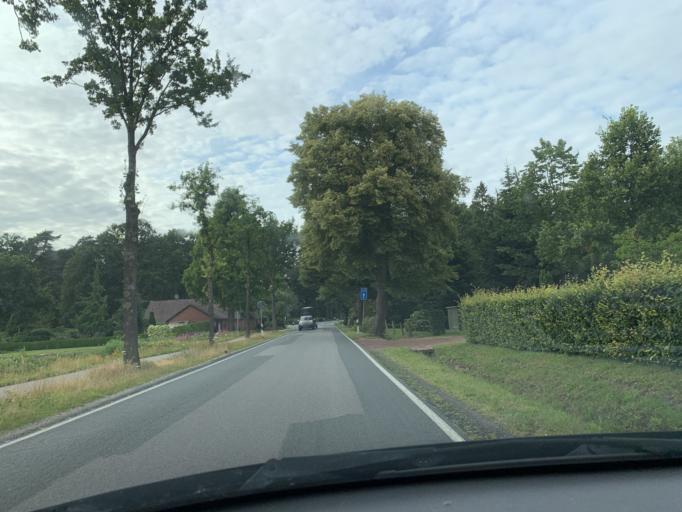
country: DE
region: Lower Saxony
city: Westerstede
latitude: 53.2864
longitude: 7.9226
